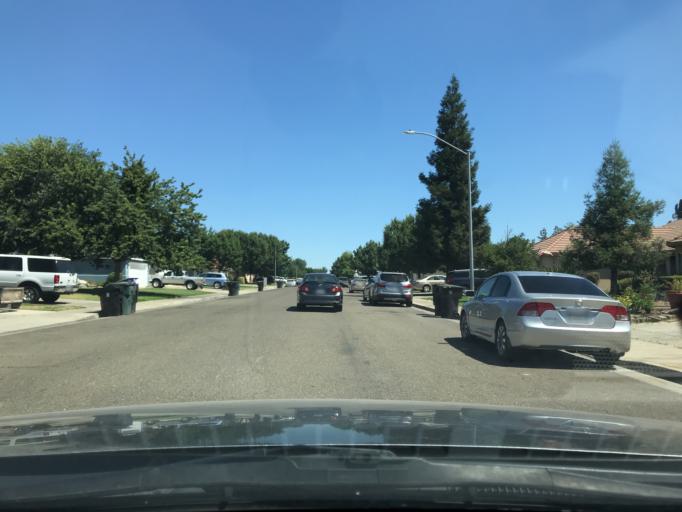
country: US
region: California
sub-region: Merced County
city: Atwater
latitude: 37.3420
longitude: -120.5859
